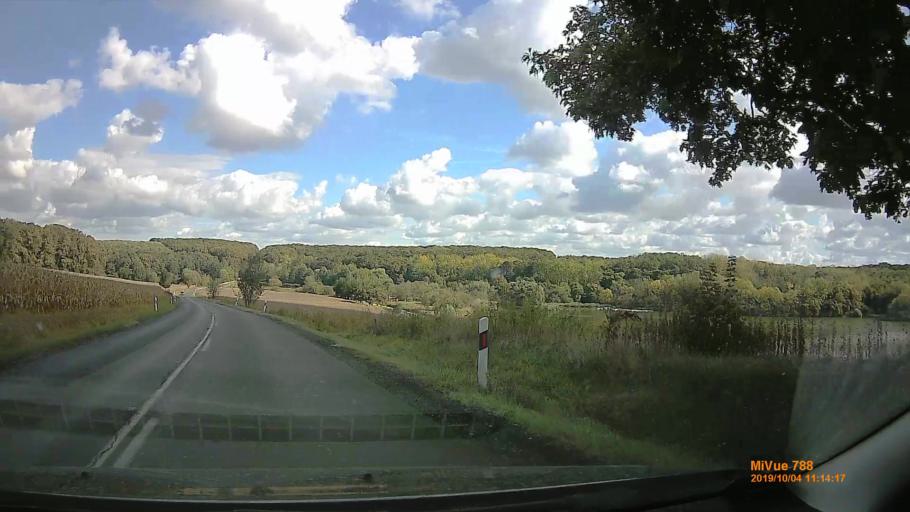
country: HU
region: Somogy
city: Kaposvar
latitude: 46.4362
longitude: 17.7911
